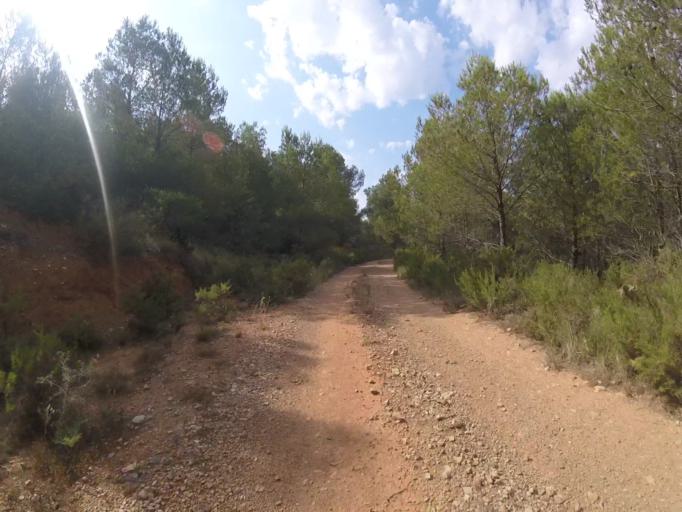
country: ES
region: Valencia
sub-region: Provincia de Castello
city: Alcala de Xivert
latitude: 40.3565
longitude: 0.1991
